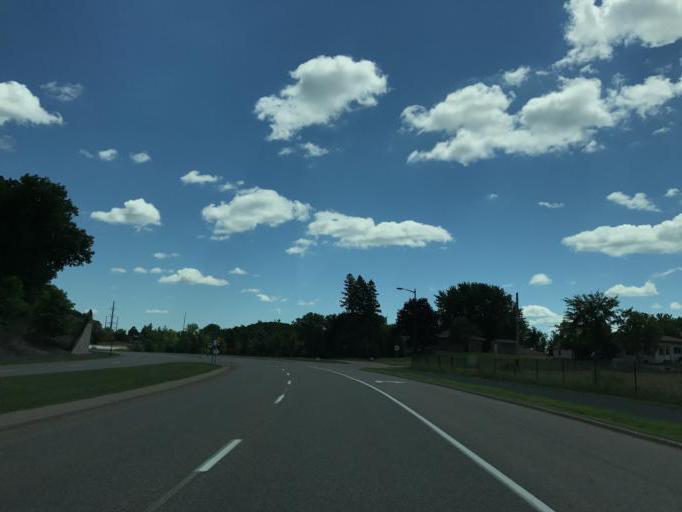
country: US
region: Minnesota
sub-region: Hennepin County
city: Maple Grove
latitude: 45.0763
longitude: -93.4683
